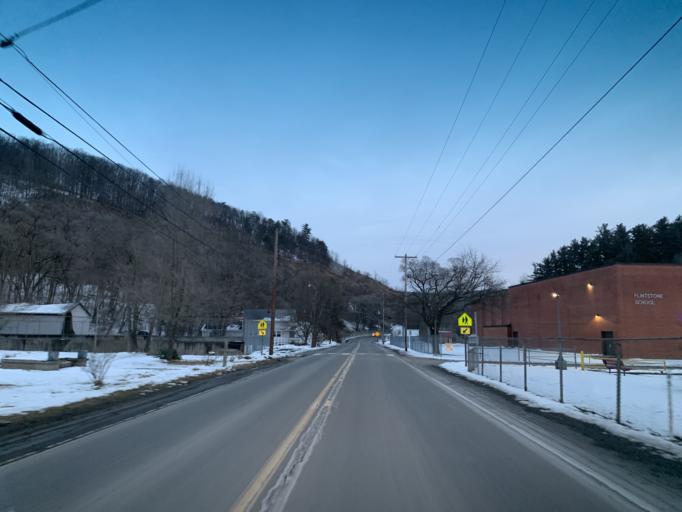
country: US
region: Maryland
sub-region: Allegany County
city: Cumberland
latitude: 39.7023
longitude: -78.5651
